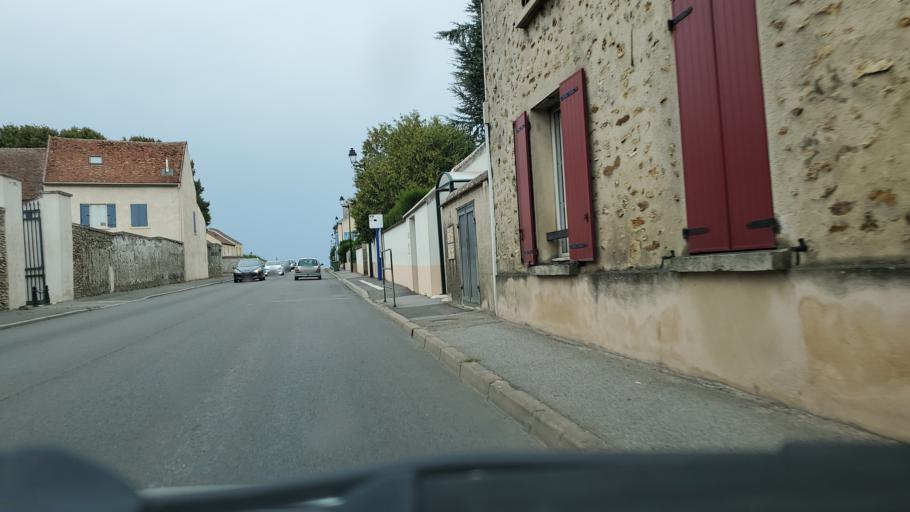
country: FR
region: Ile-de-France
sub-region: Departement de Seine-et-Marne
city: Chailly-en-Brie
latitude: 48.7900
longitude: 3.1227
